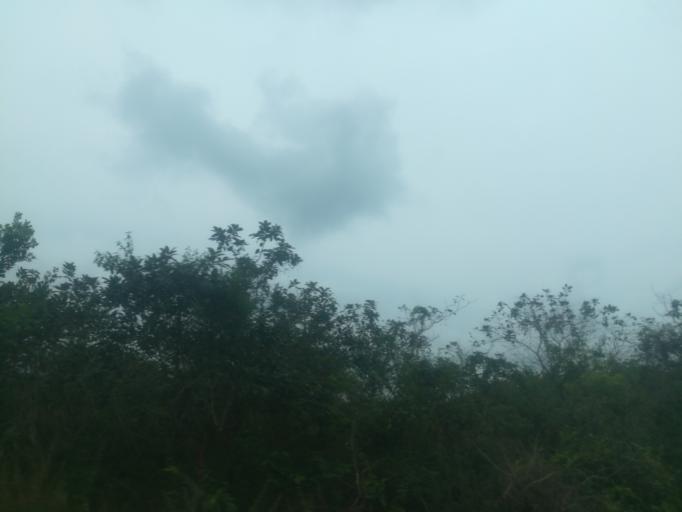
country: NG
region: Ogun
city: Ayetoro
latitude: 7.0995
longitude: 3.1278
